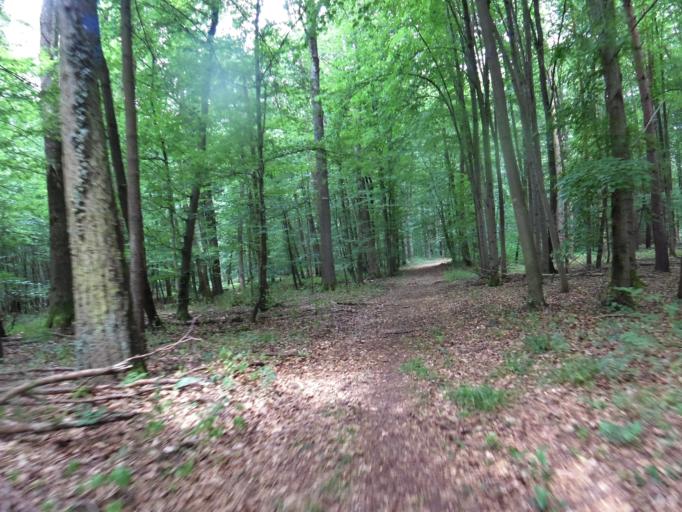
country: DE
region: Bavaria
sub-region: Regierungsbezirk Unterfranken
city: Wuerzburg
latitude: 49.7664
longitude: 9.9053
